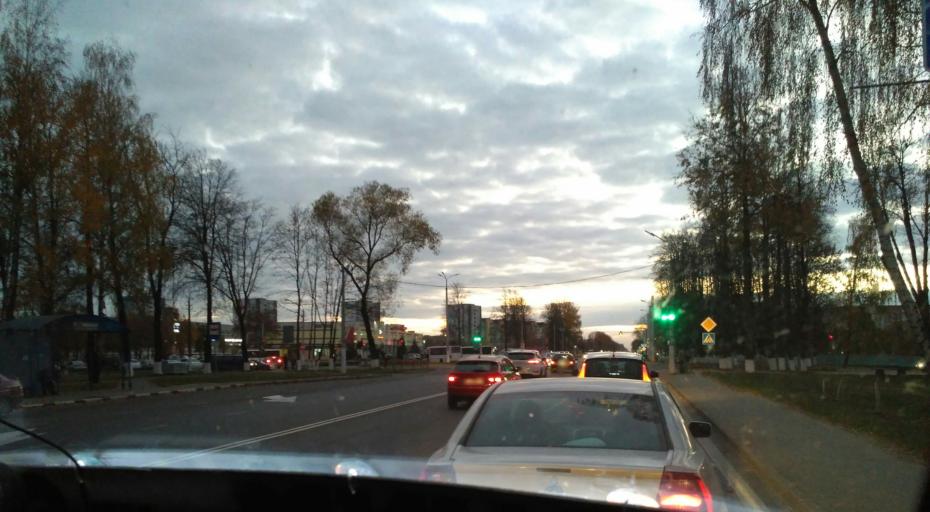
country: BY
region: Minsk
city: Horad Zhodzina
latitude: 54.0996
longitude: 28.3084
